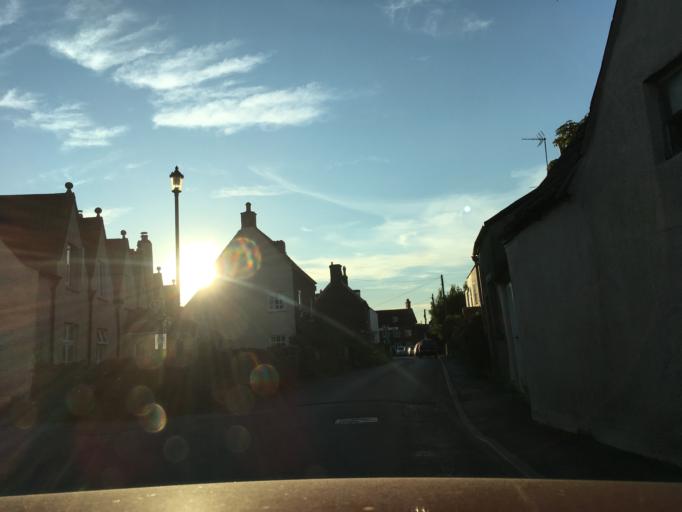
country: GB
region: England
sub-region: South Gloucestershire
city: Tytherington
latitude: 51.5503
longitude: -2.4663
